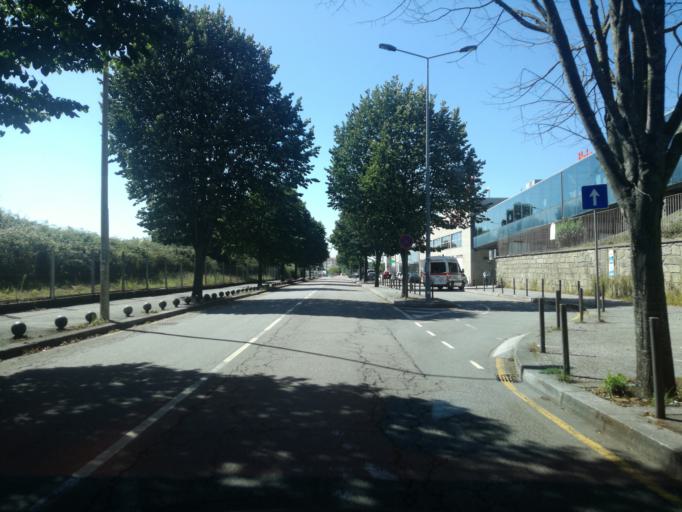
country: PT
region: Porto
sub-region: Matosinhos
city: Sao Mamede de Infesta
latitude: 41.1796
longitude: -8.6029
